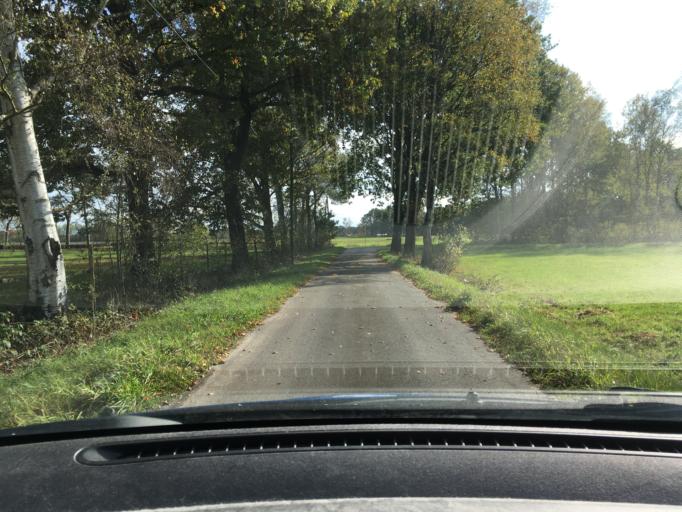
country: DE
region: Lower Saxony
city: Wistedt
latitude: 53.2527
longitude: 9.6391
